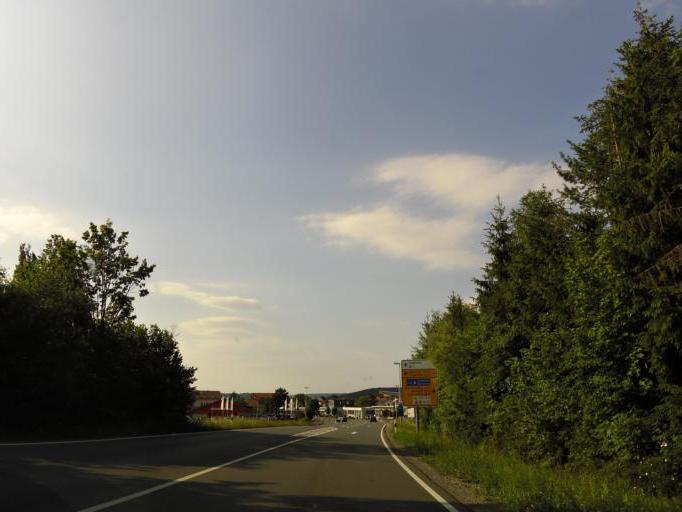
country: DE
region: Bavaria
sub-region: Regierungsbezirk Unterfranken
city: Marktheidenfeld
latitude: 49.8385
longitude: 9.6072
